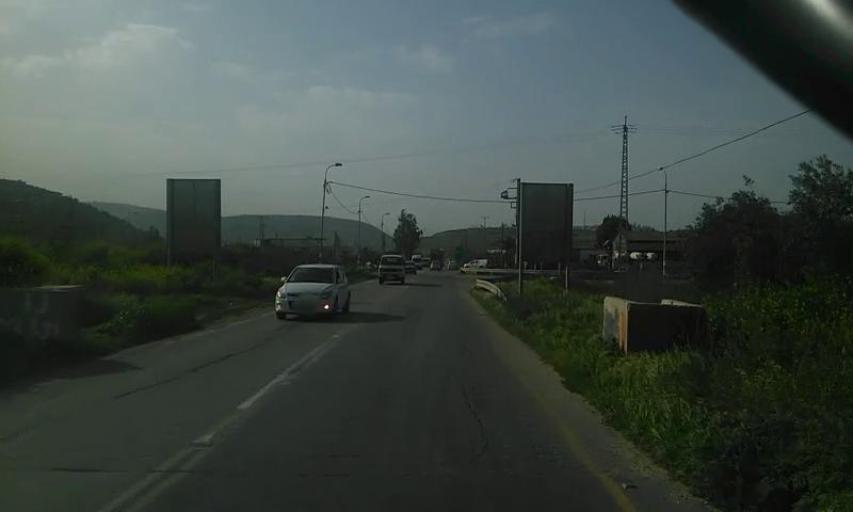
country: PS
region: West Bank
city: Dayr Sharaf
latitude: 32.2642
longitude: 35.1710
